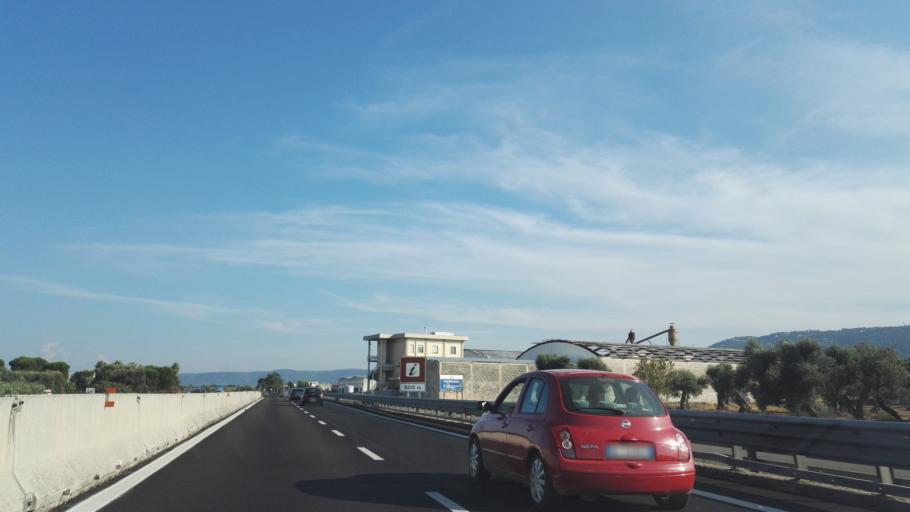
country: IT
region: Apulia
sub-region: Provincia di Brindisi
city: Fasano
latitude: 40.8611
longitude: 17.3482
